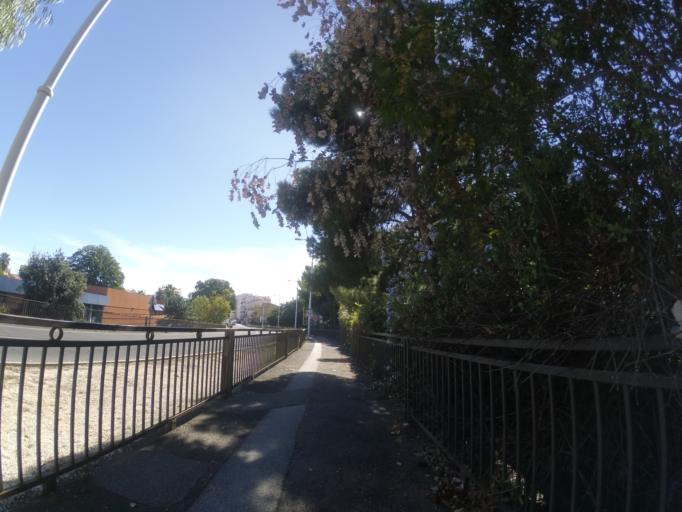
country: FR
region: Languedoc-Roussillon
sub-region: Departement des Pyrenees-Orientales
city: Perpignan
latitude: 42.7050
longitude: 2.8825
